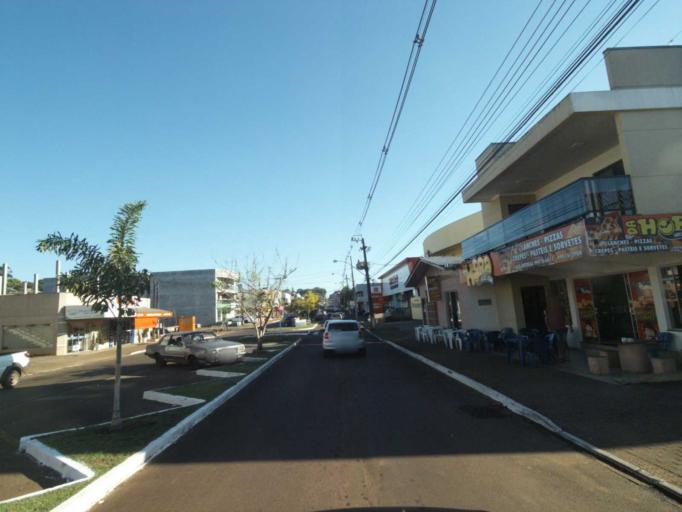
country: BR
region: Parana
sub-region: Coronel Vivida
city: Coronel Vivida
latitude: -25.9667
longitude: -52.8147
